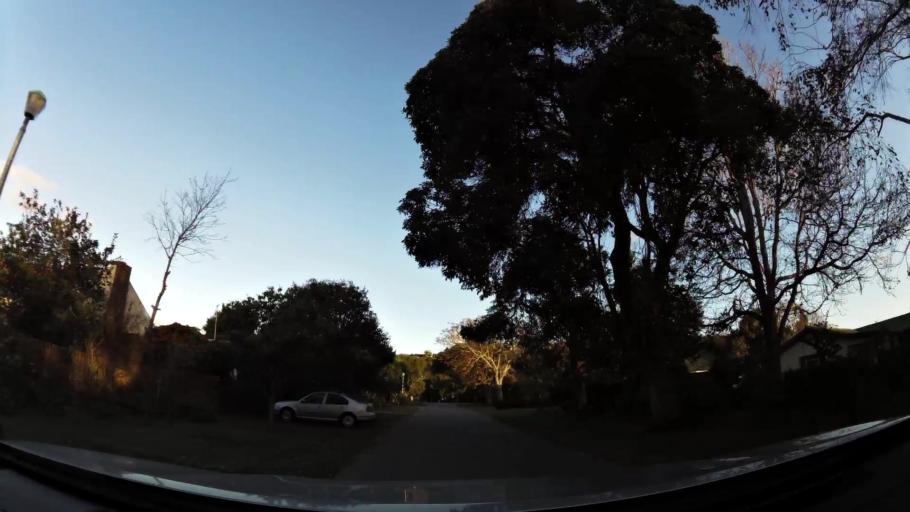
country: ZA
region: Western Cape
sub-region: Eden District Municipality
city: Knysna
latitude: -34.0193
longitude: 22.8045
